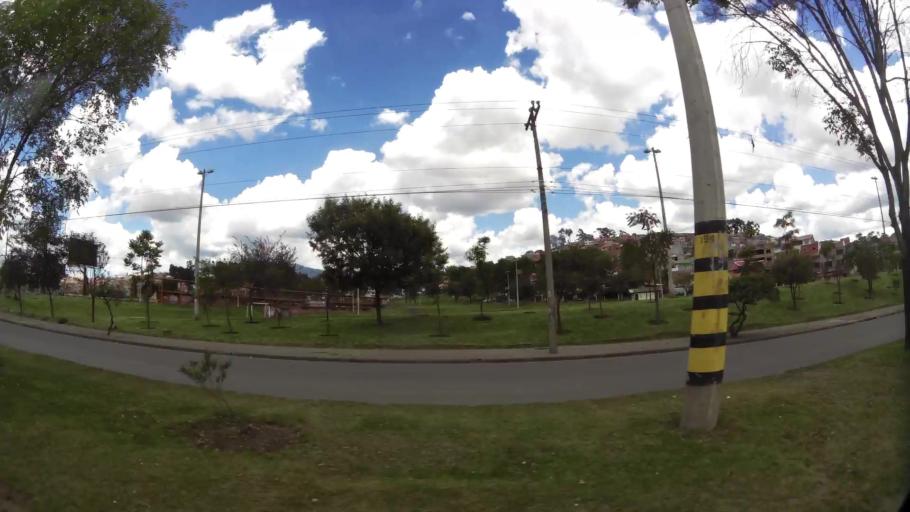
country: EC
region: Azuay
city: Cuenca
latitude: -2.8850
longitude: -78.9921
